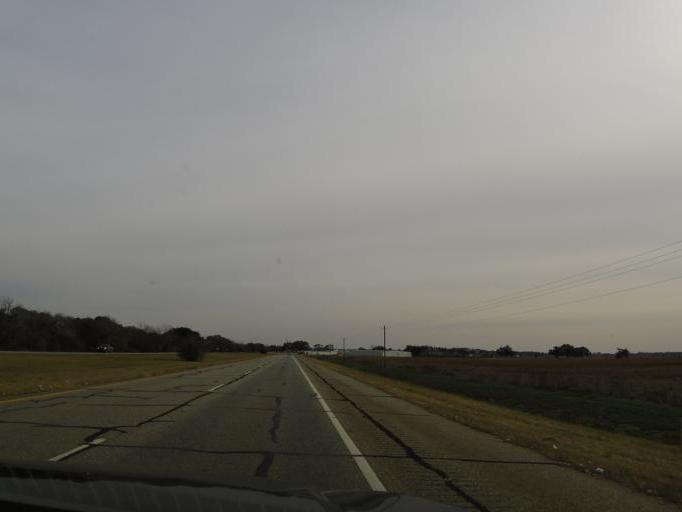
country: US
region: Georgia
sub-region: Seminole County
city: Donalsonville
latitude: 31.0519
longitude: -84.9039
